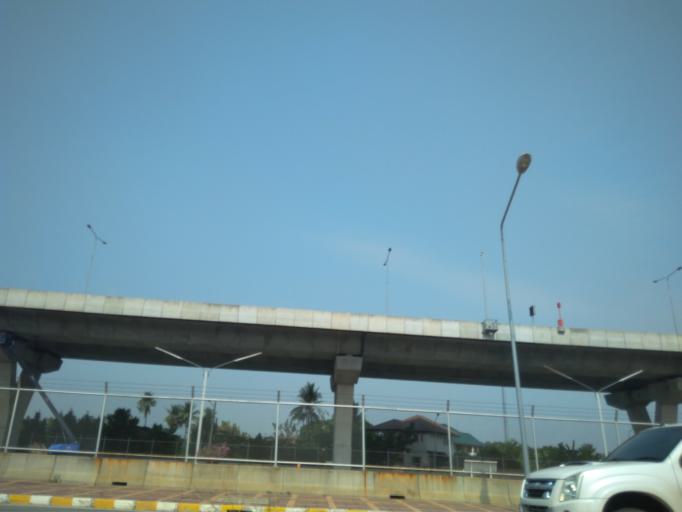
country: TH
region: Bangkok
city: Taling Chan
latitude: 13.7900
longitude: 100.4386
